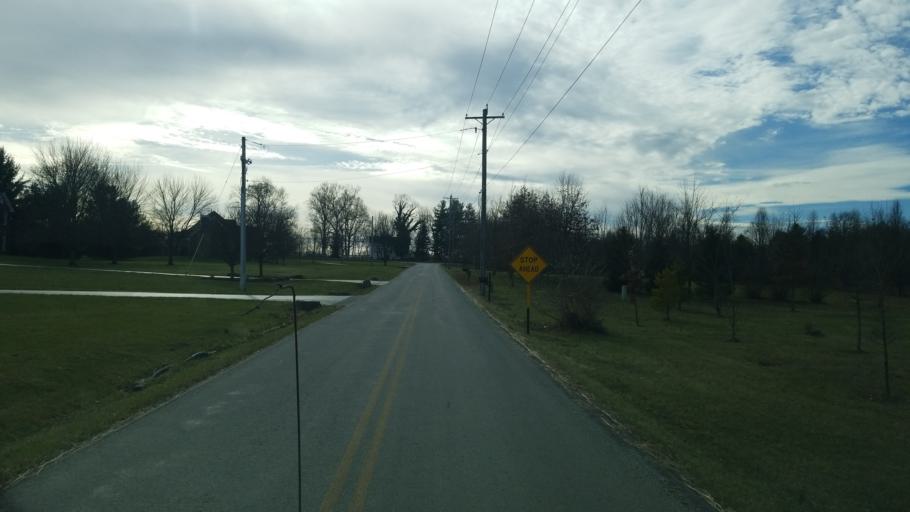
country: US
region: Ohio
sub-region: Warren County
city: Lebanon
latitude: 39.4204
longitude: -84.1603
